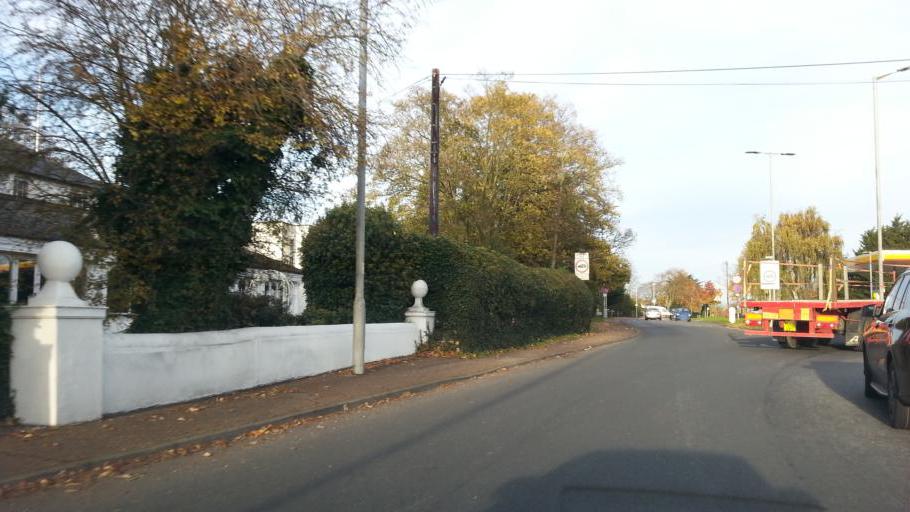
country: GB
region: England
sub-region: Hertfordshire
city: St Albans
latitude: 51.7207
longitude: -0.3649
